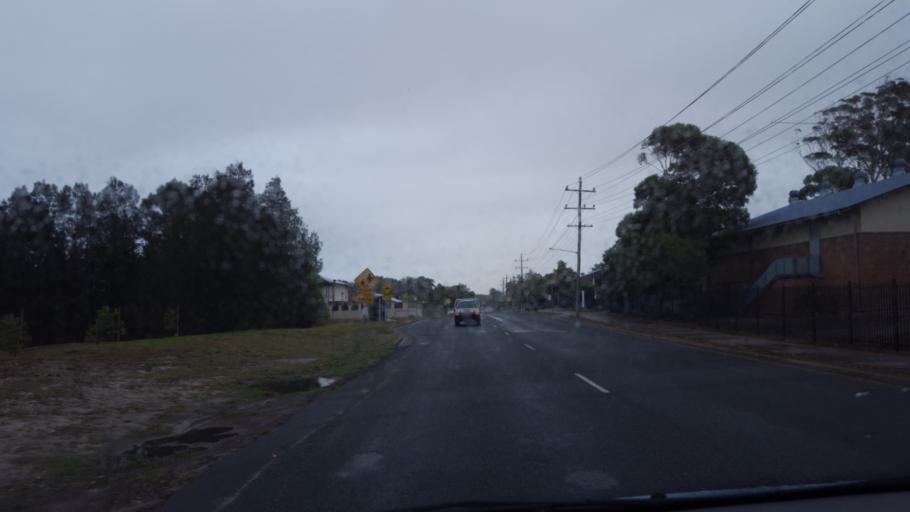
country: AU
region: New South Wales
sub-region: Port Stephens Shire
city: Anna Bay
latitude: -32.7767
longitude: 152.0912
